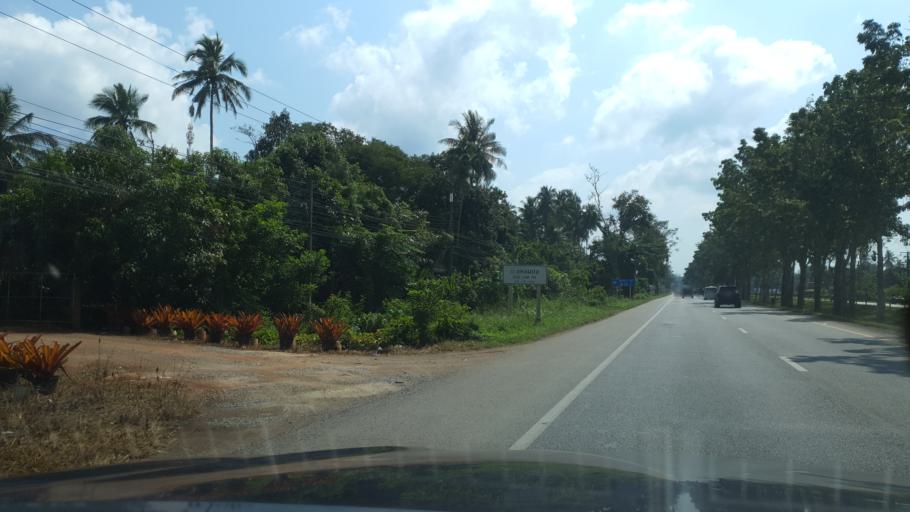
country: TH
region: Chumphon
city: Sawi
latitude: 10.2376
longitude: 99.0950
